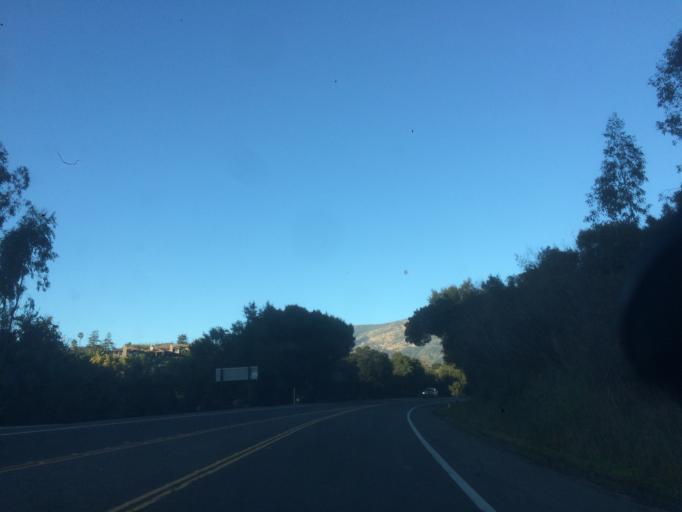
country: US
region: California
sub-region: Santa Barbara County
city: Mission Canyon
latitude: 34.4187
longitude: -119.7412
